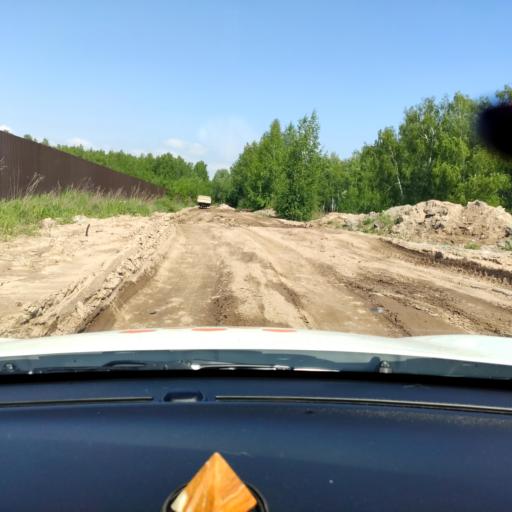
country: RU
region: Tatarstan
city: Stolbishchi
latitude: 55.7047
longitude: 49.1815
